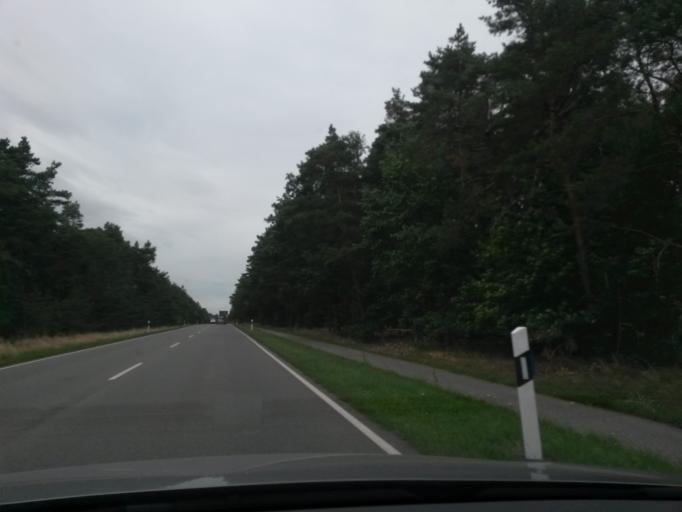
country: DE
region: Saxony-Anhalt
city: Klietz
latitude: 52.6772
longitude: 12.0638
